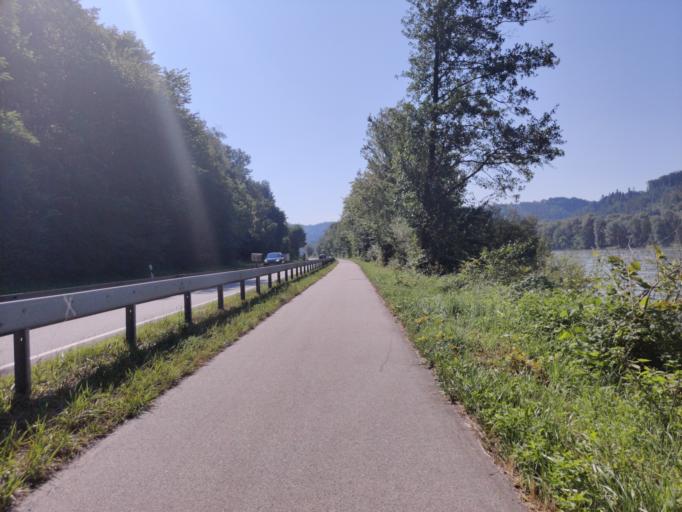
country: DE
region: Bavaria
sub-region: Lower Bavaria
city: Thyrnau
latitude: 48.5754
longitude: 13.5459
